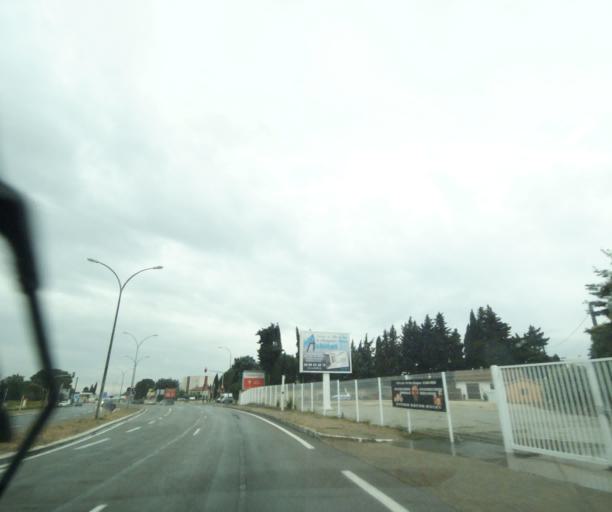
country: FR
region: Languedoc-Roussillon
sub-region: Departement du Gard
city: Rodilhan
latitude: 43.8529
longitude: 4.4006
